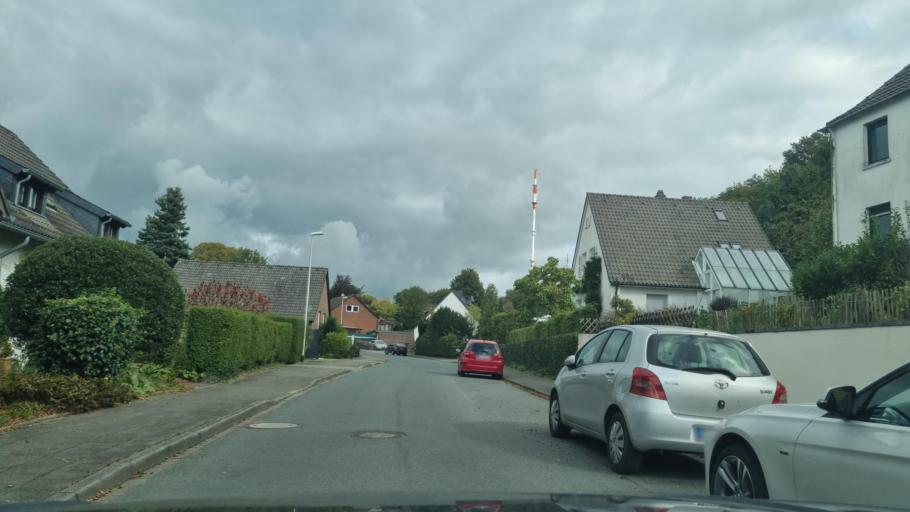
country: DE
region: North Rhine-Westphalia
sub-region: Regierungsbezirk Dusseldorf
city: Kleve
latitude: 51.7836
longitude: 6.1054
